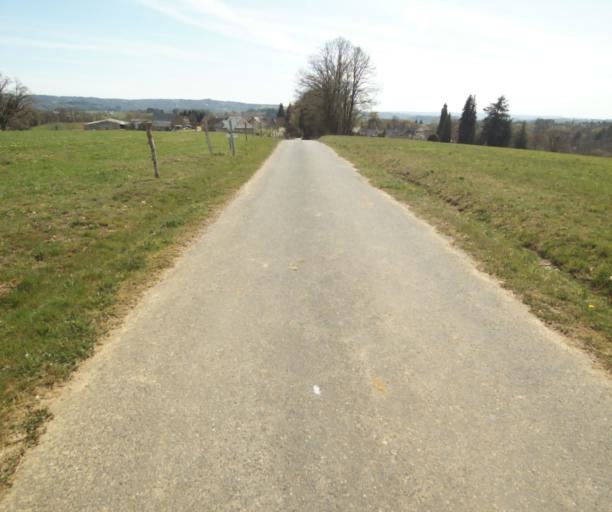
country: FR
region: Limousin
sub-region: Departement de la Correze
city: Correze
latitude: 45.3843
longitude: 1.8081
